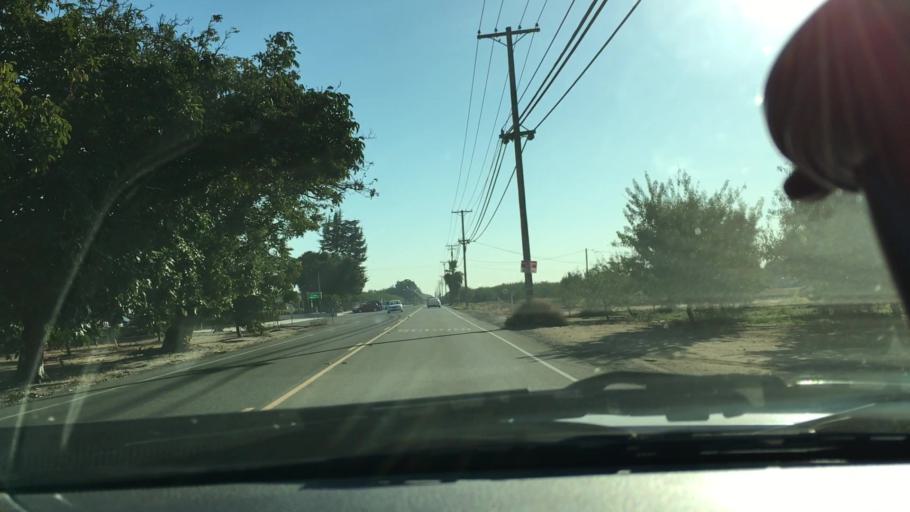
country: US
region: California
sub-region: Stanislaus County
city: Bret Harte
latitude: 37.5950
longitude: -121.0239
